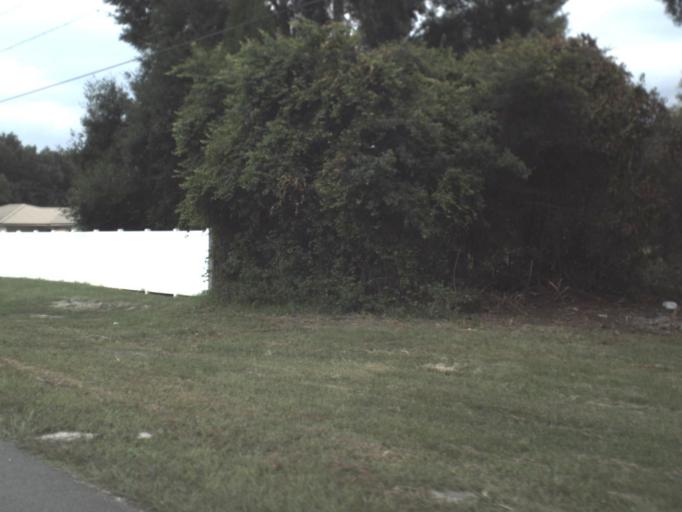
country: US
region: Florida
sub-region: Pasco County
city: Shady Hills
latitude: 28.3554
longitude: -82.5043
